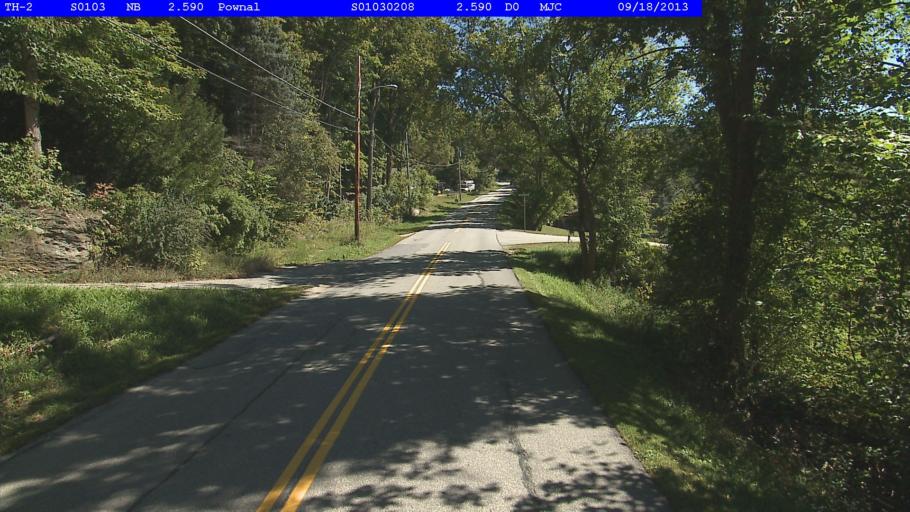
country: US
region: Vermont
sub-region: Bennington County
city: Bennington
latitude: 42.7970
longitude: -73.2275
